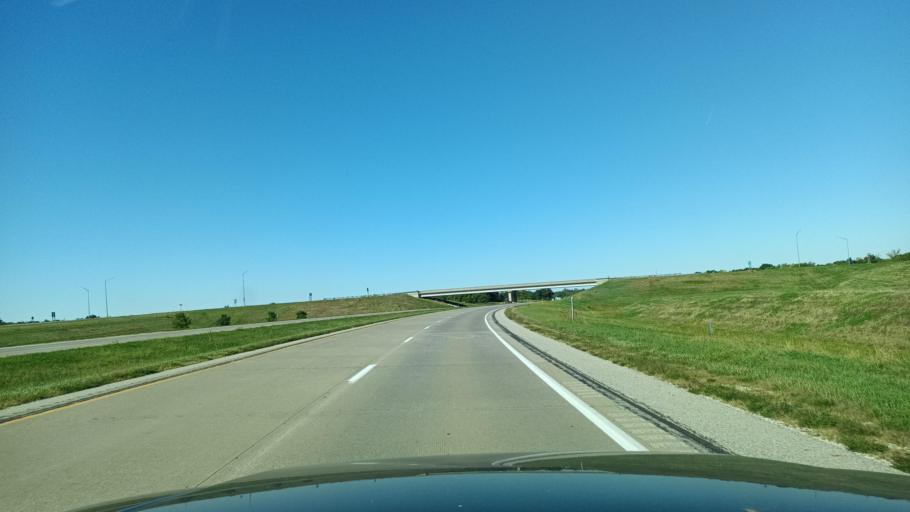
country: US
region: Iowa
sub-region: Lee County
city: Fort Madison
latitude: 40.6711
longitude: -91.2687
